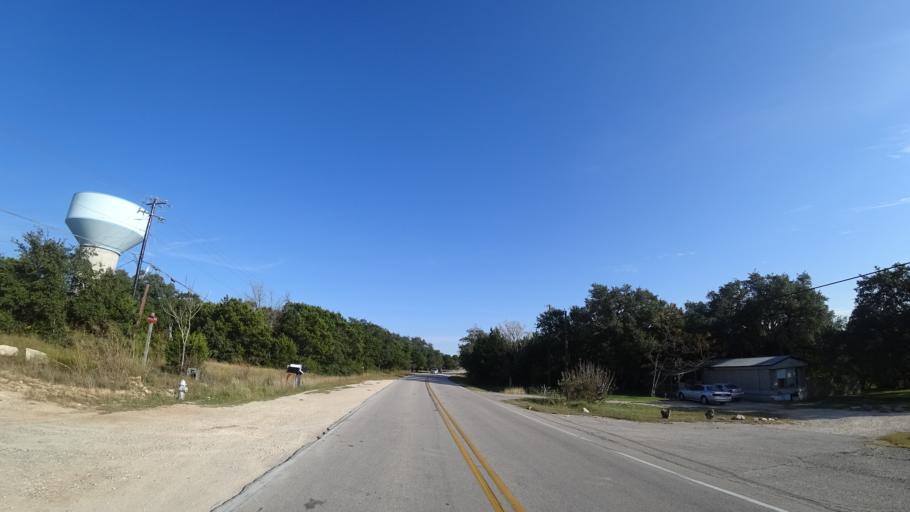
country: US
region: Texas
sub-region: Travis County
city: Bee Cave
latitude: 30.2461
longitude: -97.9269
